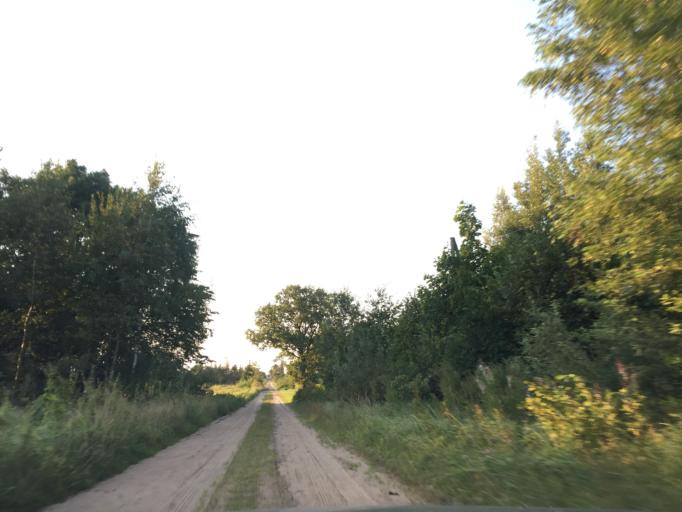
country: LV
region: Limbazu Rajons
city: Limbazi
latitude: 57.5656
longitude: 24.7725
